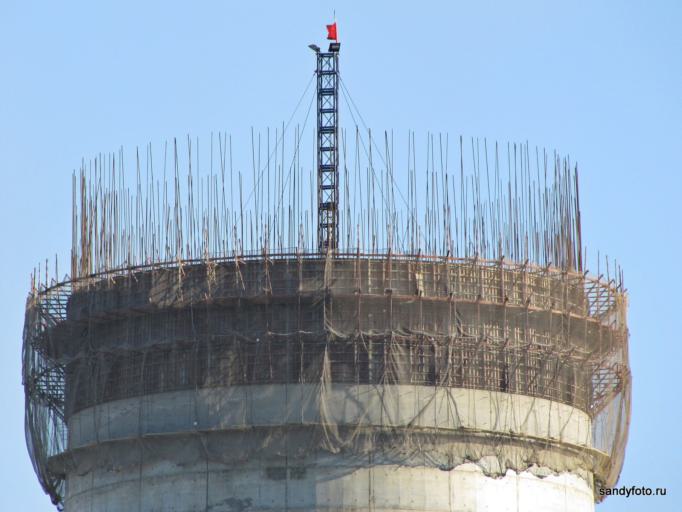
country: RU
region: Chelyabinsk
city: Bobrovka
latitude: 54.0405
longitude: 61.6588
